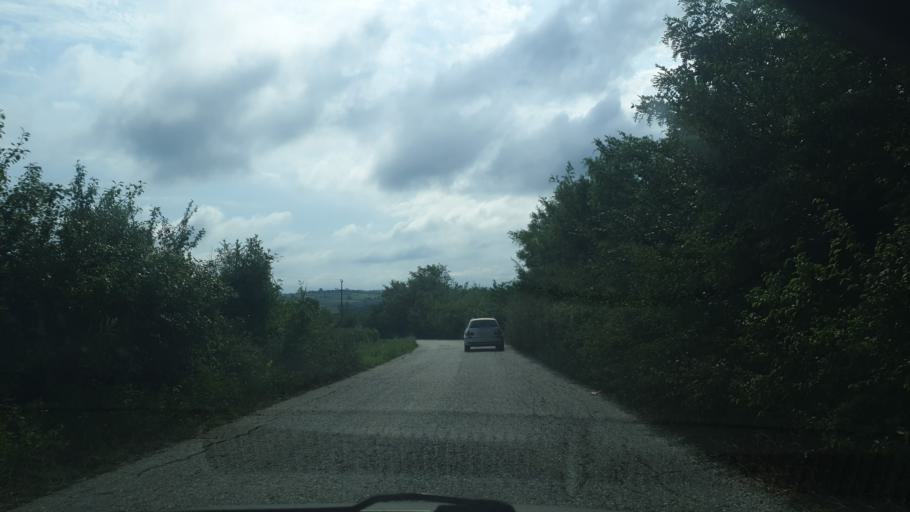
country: RS
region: Central Serbia
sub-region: Sumadijski Okrug
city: Kragujevac
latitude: 44.0960
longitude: 20.7876
